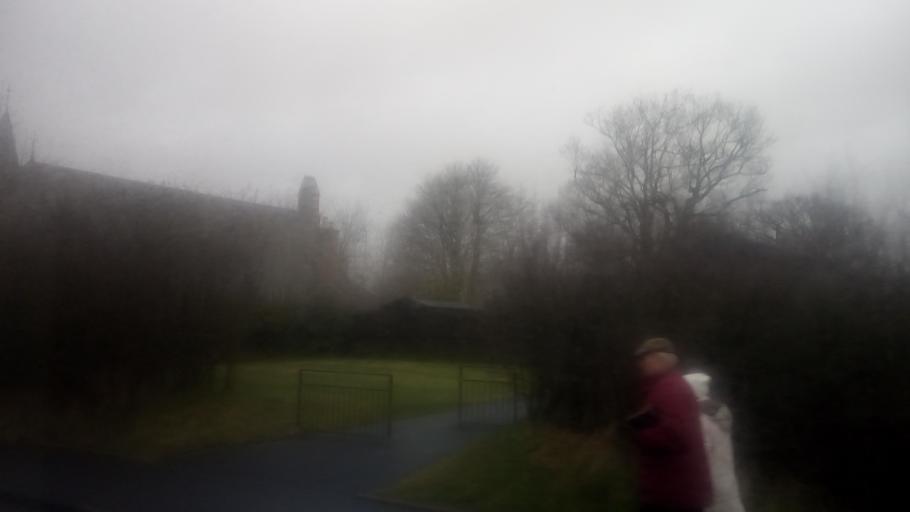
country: GB
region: Scotland
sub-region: The Scottish Borders
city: Newtown St Boswells
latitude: 55.5751
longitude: -2.6665
